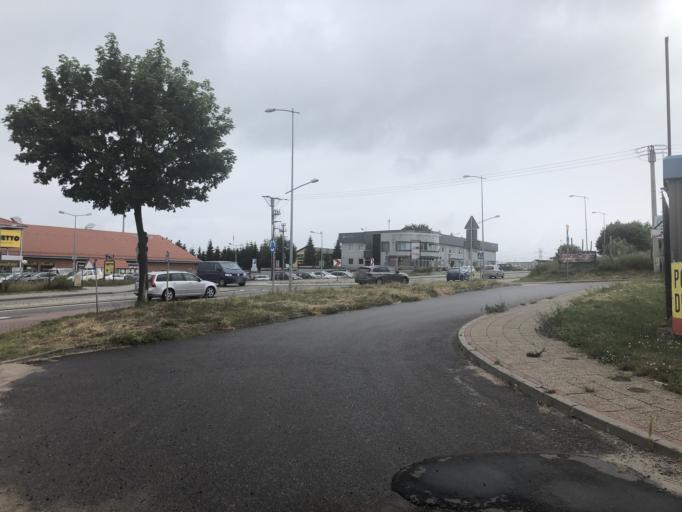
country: PL
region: Pomeranian Voivodeship
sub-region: Powiat gdanski
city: Rotmanka
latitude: 54.2785
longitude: 18.5950
